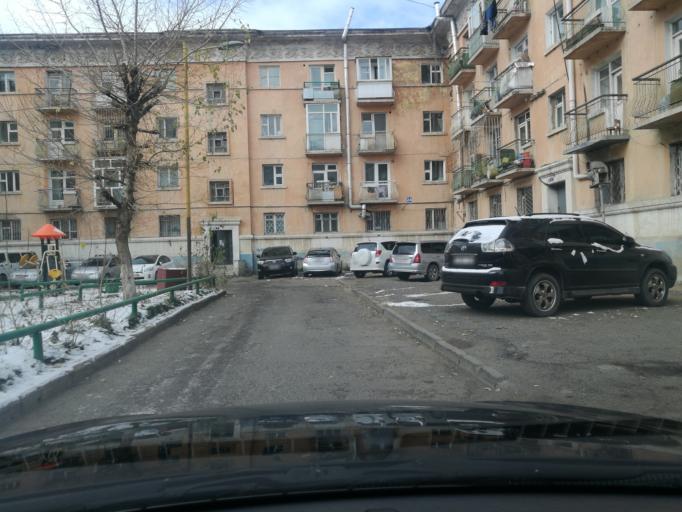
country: MN
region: Ulaanbaatar
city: Ulaanbaatar
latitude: 47.9153
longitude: 106.8995
